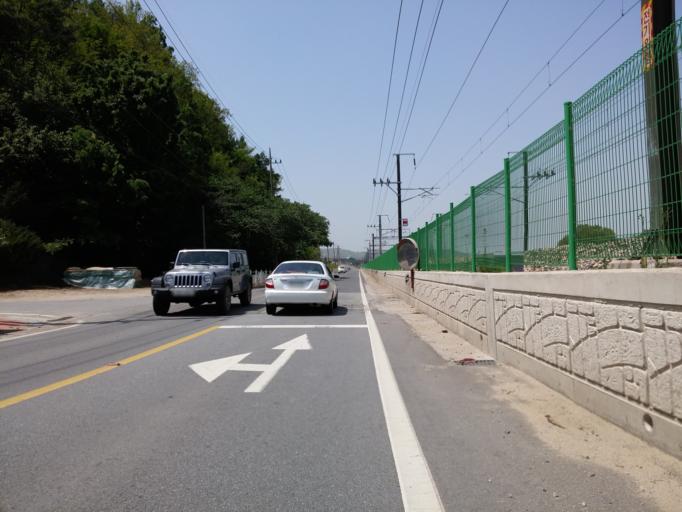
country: KR
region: Chungcheongnam-do
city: Nonsan
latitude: 36.2156
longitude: 127.2117
